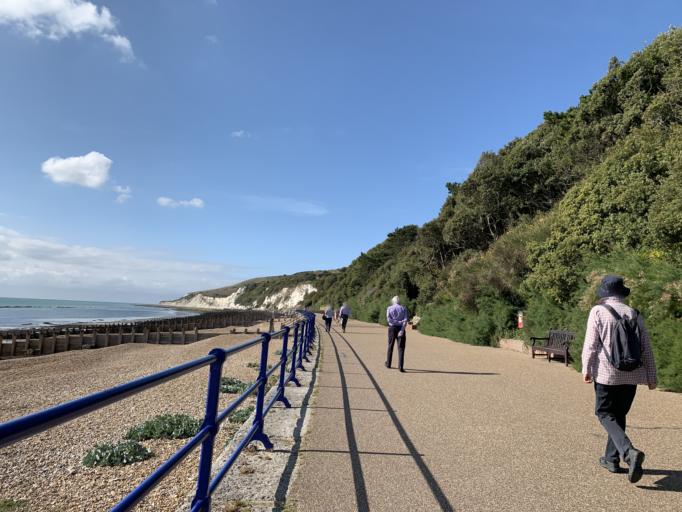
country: GB
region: England
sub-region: East Sussex
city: Eastbourne
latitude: 50.7560
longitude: 0.2768
